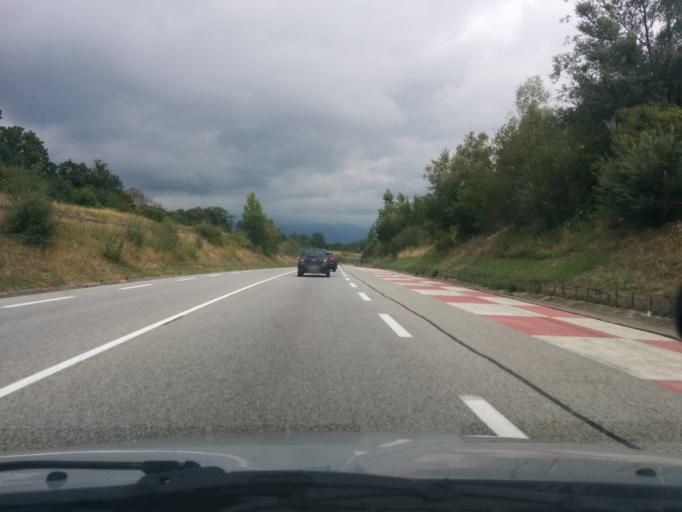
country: FR
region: Rhone-Alpes
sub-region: Departement de l'Isere
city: Voiron
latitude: 45.3841
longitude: 5.5745
